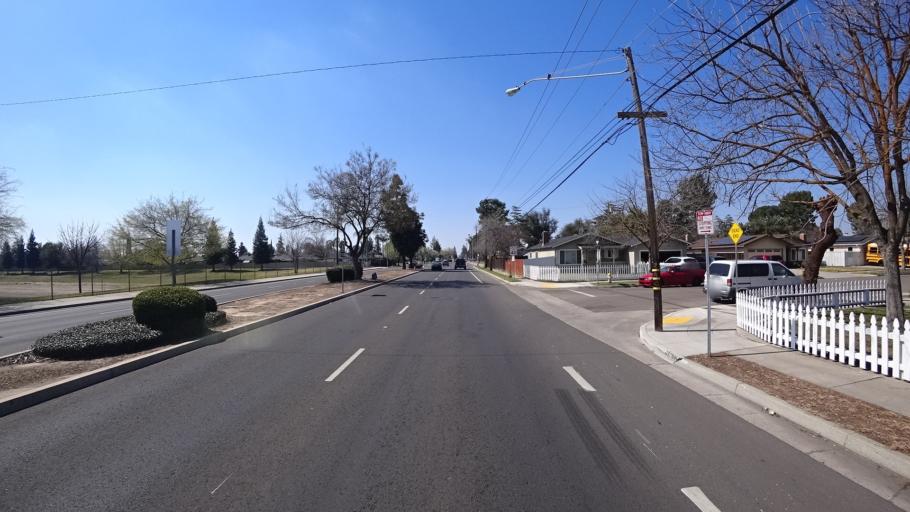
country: US
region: California
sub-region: Fresno County
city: Fresno
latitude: 36.7938
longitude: -119.8385
